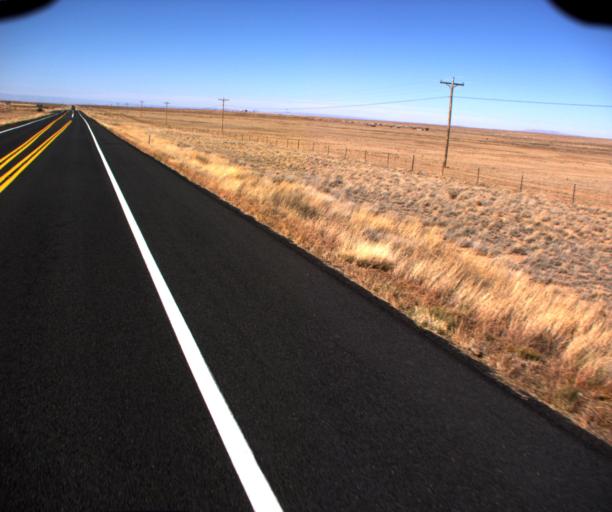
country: US
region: Arizona
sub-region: Coconino County
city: Tuba City
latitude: 35.9965
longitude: -111.0267
